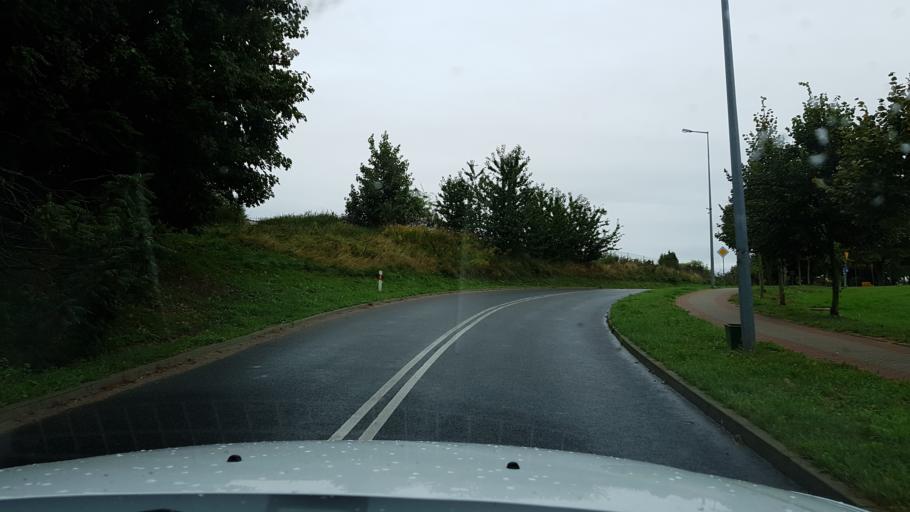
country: PL
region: West Pomeranian Voivodeship
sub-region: Powiat gryfinski
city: Cedynia
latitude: 52.8804
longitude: 14.2127
